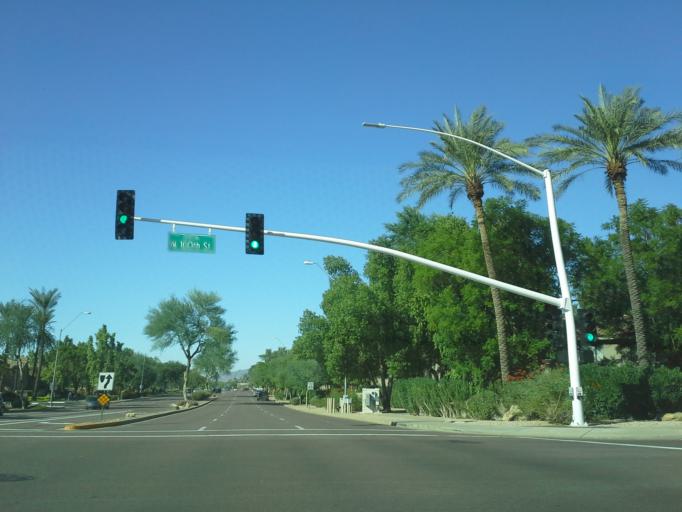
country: US
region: Arizona
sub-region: Maricopa County
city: Paradise Valley
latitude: 33.6243
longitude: -111.8717
